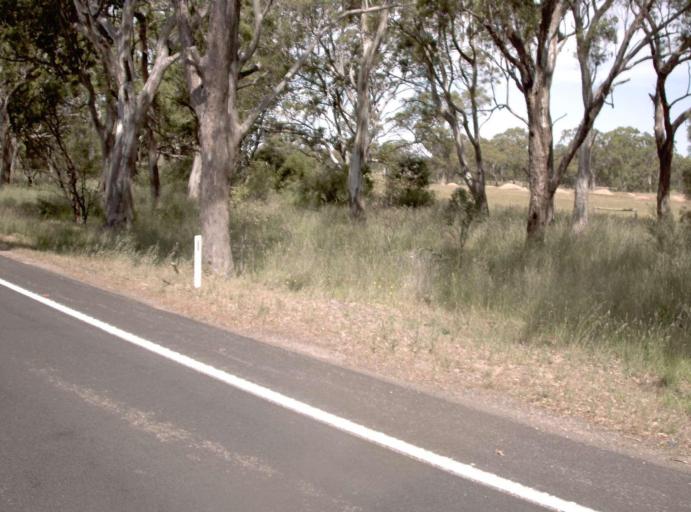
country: AU
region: Victoria
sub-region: Wellington
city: Sale
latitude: -37.9265
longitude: 147.2199
